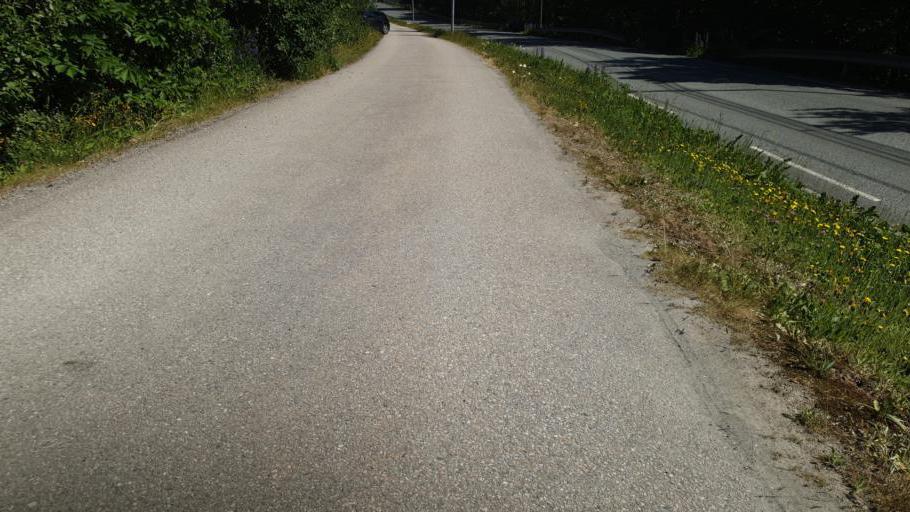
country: NO
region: Sor-Trondelag
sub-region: Trondheim
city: Trondheim
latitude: 63.5564
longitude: 10.2338
